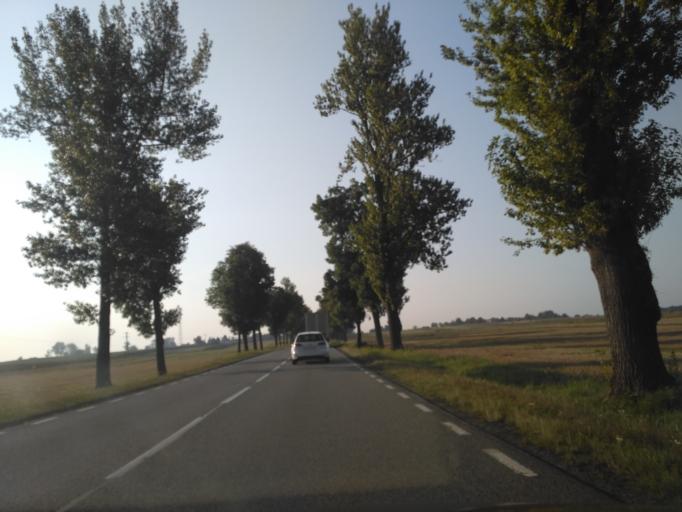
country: PL
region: Lublin Voivodeship
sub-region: Powiat krasnicki
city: Szastarka
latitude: 50.8403
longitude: 22.2989
